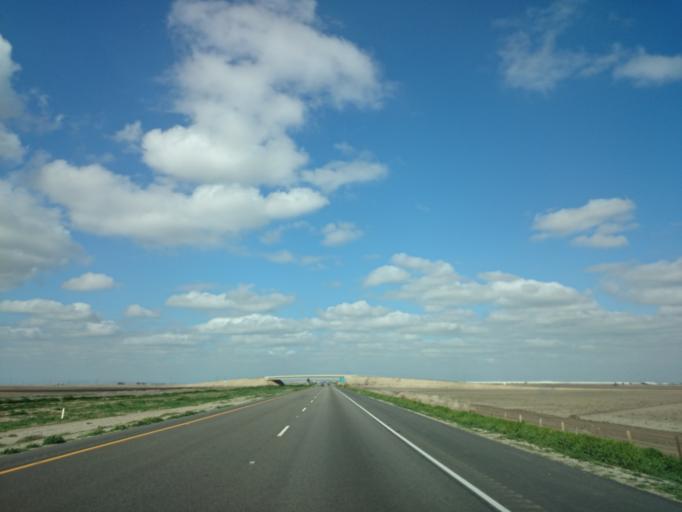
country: US
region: California
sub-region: Kern County
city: Greenfield
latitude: 35.1487
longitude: -119.0962
